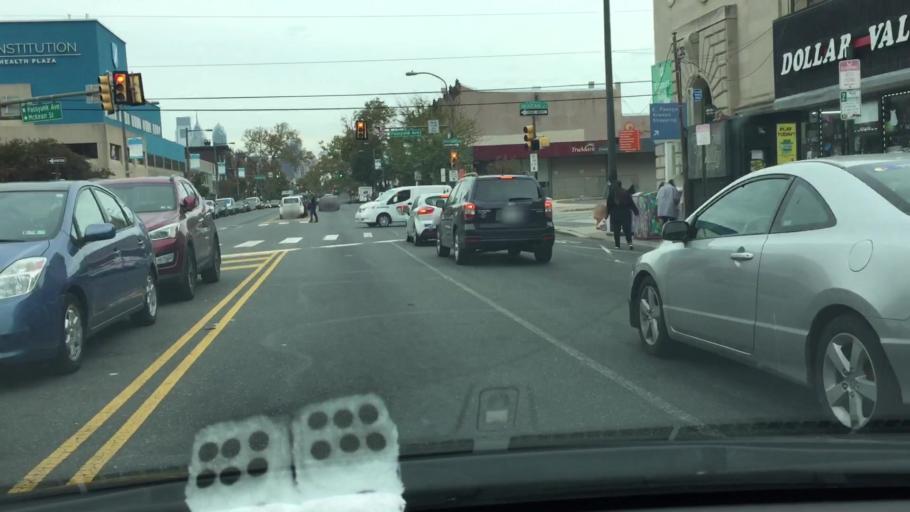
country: US
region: Pennsylvania
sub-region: Philadelphia County
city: Philadelphia
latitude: 39.9252
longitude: -75.1695
